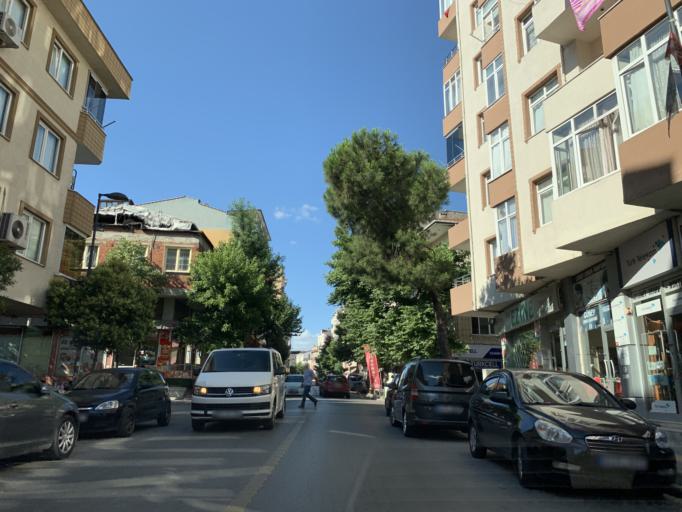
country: TR
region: Istanbul
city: Pendik
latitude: 40.8741
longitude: 29.2686
